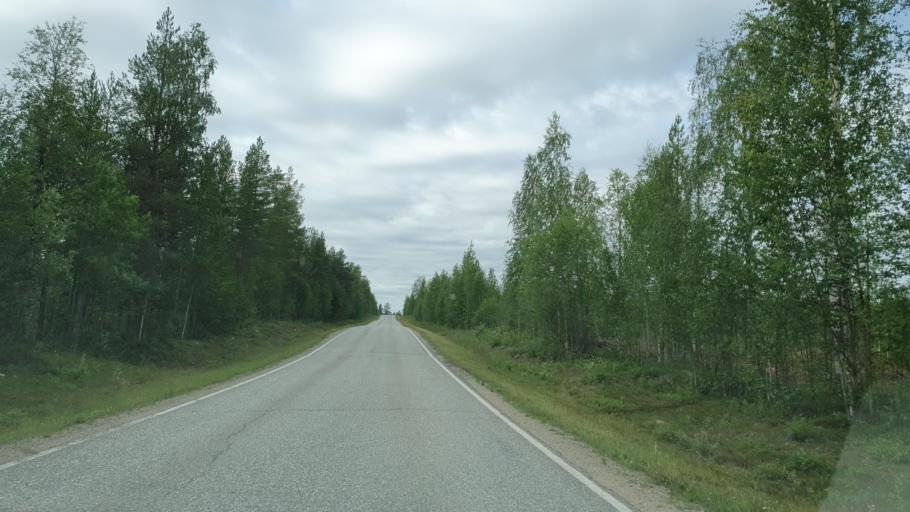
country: FI
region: Lapland
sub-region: Tunturi-Lappi
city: Kittilae
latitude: 67.6112
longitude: 25.2407
